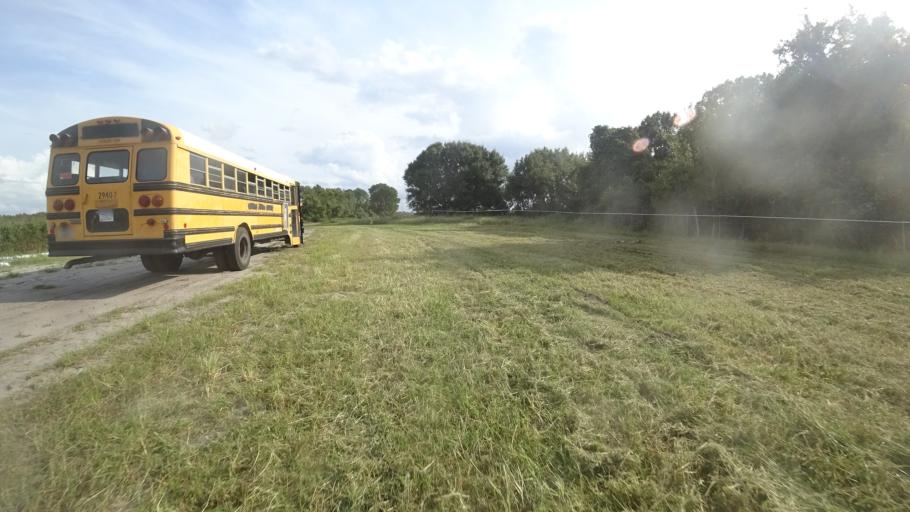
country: US
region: Florida
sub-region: Hillsborough County
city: Wimauma
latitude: 27.5966
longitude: -82.1490
